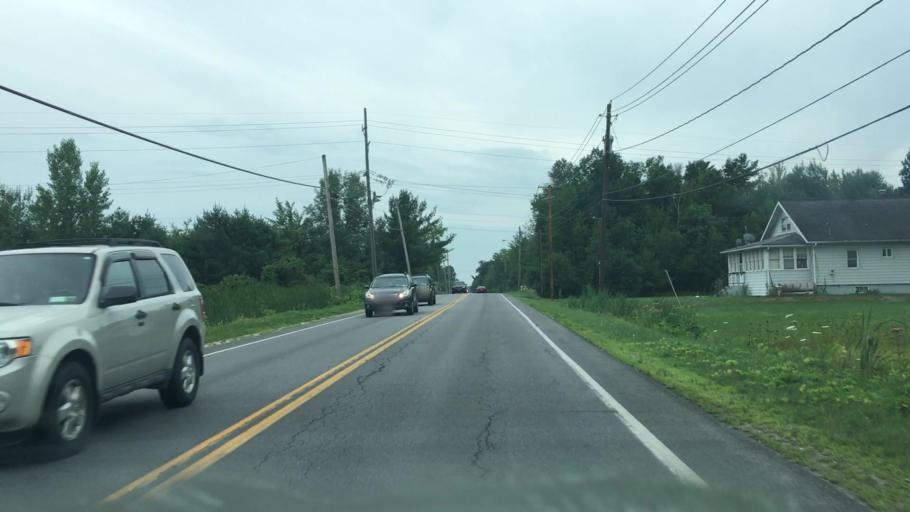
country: US
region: New York
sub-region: Clinton County
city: Plattsburgh West
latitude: 44.6639
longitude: -73.5085
